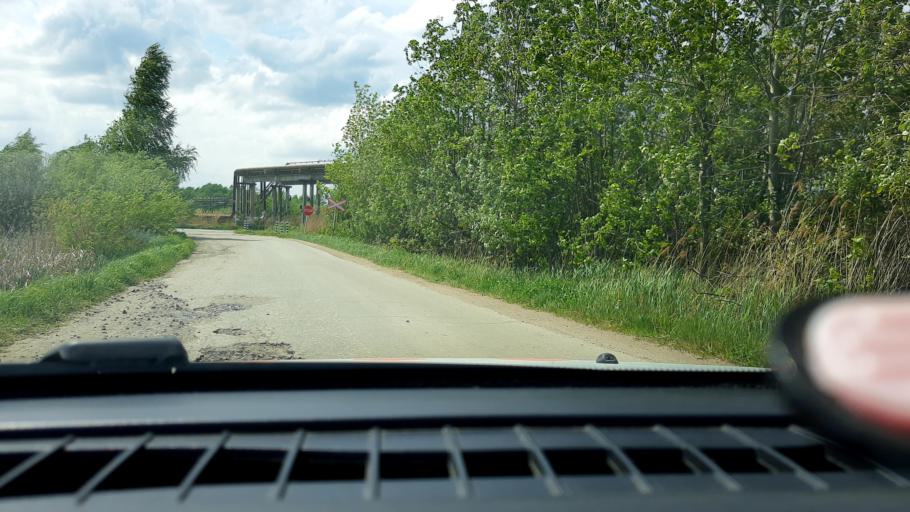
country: RU
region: Nizjnij Novgorod
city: Kstovo
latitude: 56.1348
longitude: 44.1271
